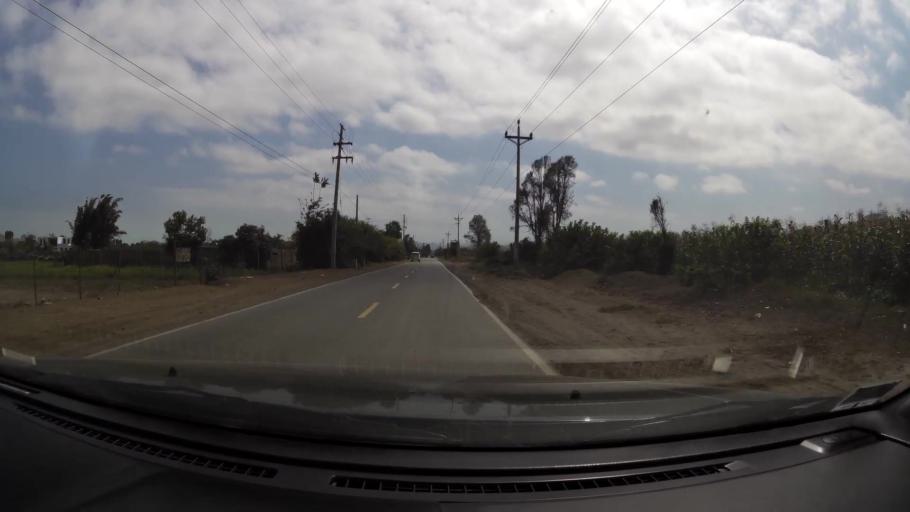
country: PE
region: Lima
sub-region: Provincia de Canete
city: Mala
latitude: -12.7026
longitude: -76.6225
